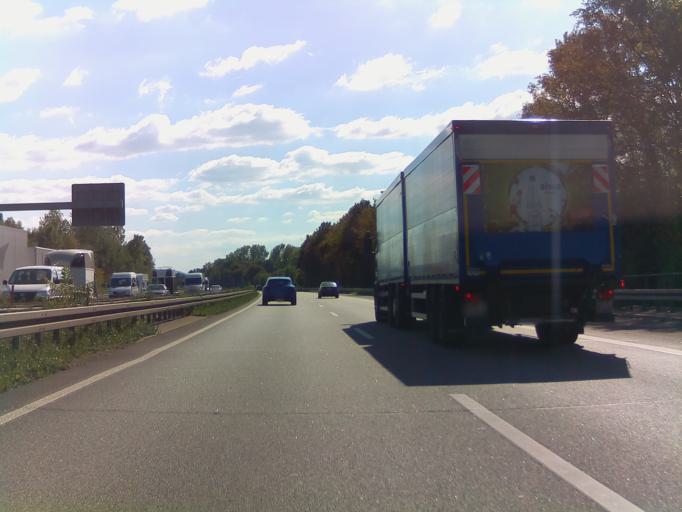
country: DE
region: Hesse
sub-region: Regierungsbezirk Darmstadt
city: Heppenheim an der Bergstrasse
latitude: 49.6377
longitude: 8.6099
